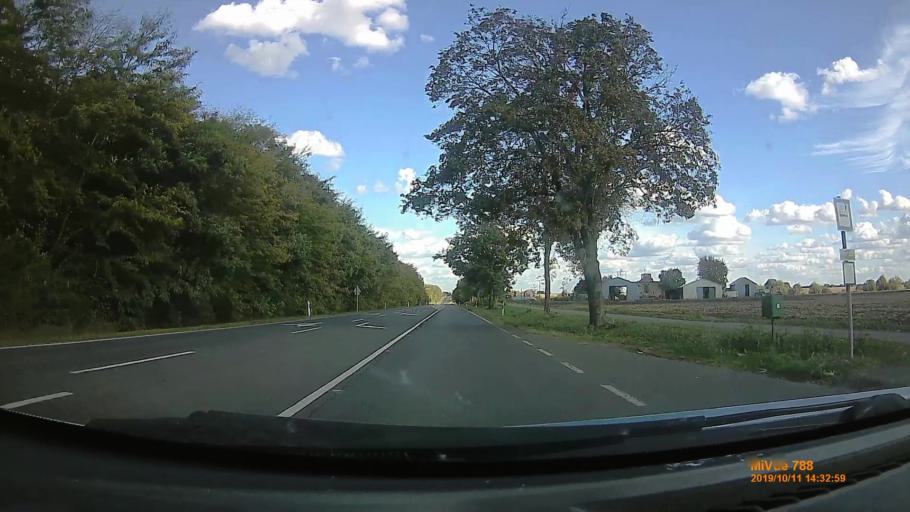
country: HU
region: Hajdu-Bihar
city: Ebes
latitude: 47.5624
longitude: 21.4478
